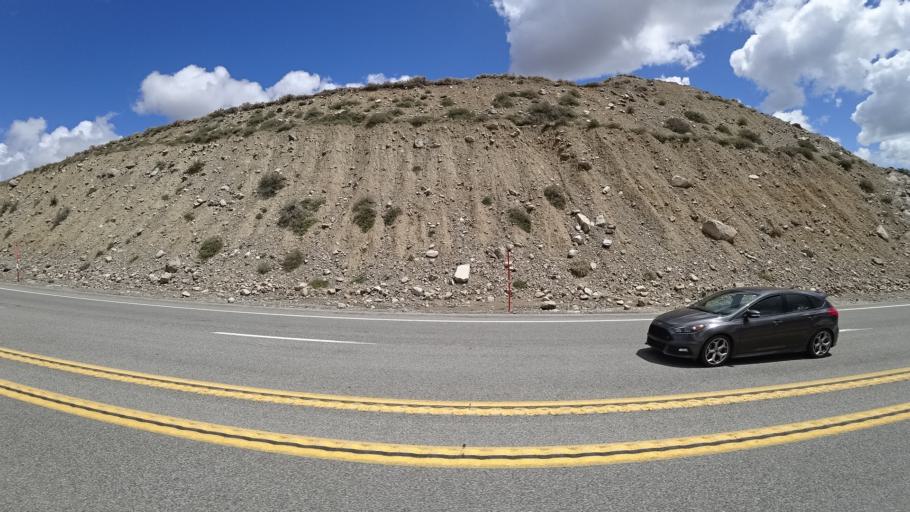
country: US
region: California
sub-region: Mono County
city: Bridgeport
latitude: 38.0763
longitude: -119.1788
